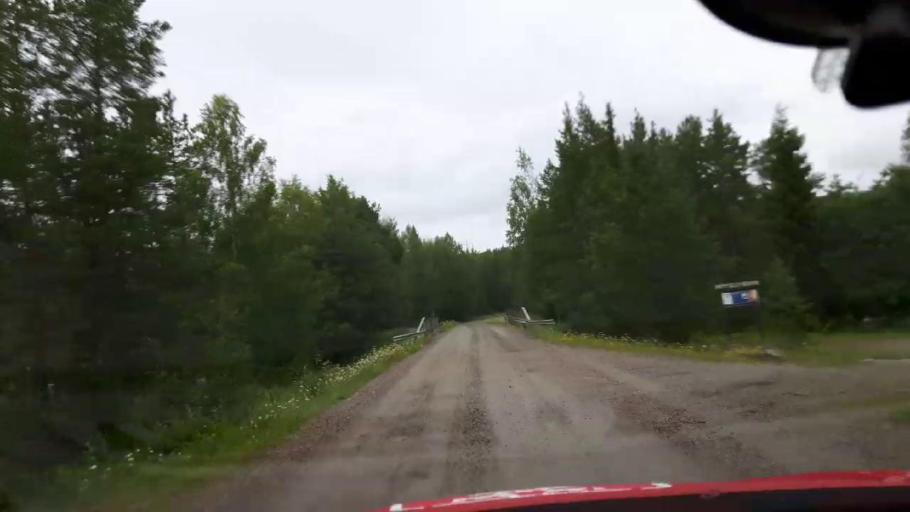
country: SE
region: Jaemtland
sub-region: OEstersunds Kommun
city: Brunflo
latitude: 62.8136
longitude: 14.8828
